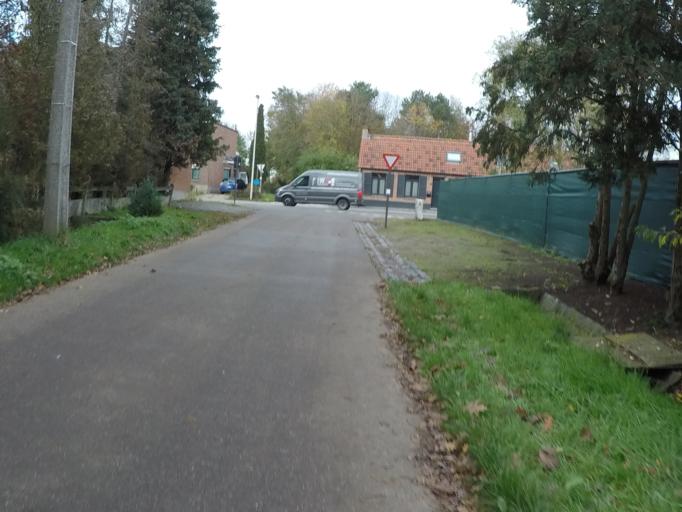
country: BE
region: Flanders
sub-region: Provincie Antwerpen
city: Nijlen
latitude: 51.1325
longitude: 4.6957
